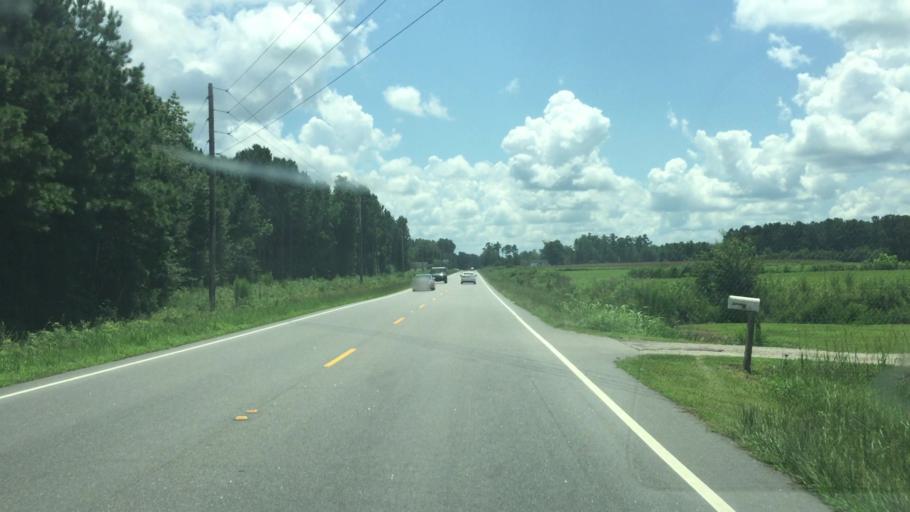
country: US
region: North Carolina
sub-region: Columbus County
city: Tabor City
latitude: 34.2252
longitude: -78.8243
